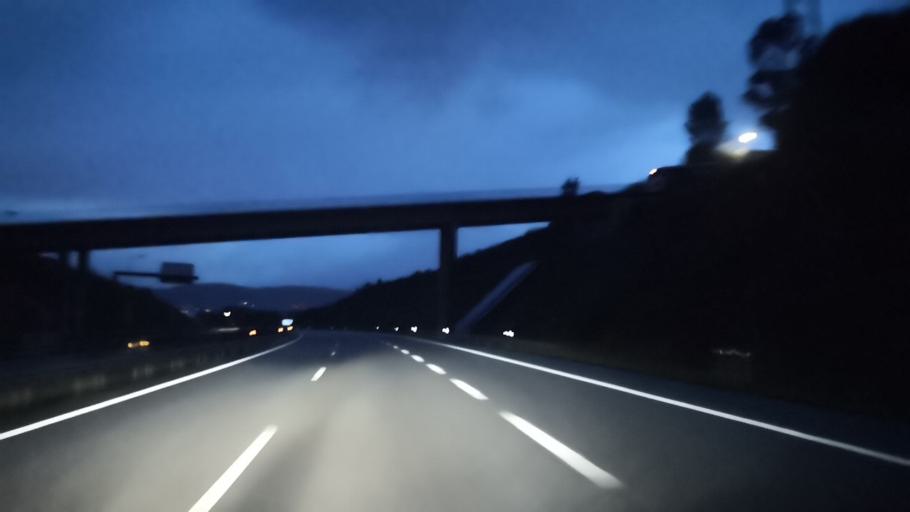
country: PT
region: Braga
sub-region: Guimaraes
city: Candoso
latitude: 41.4451
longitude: -8.3291
